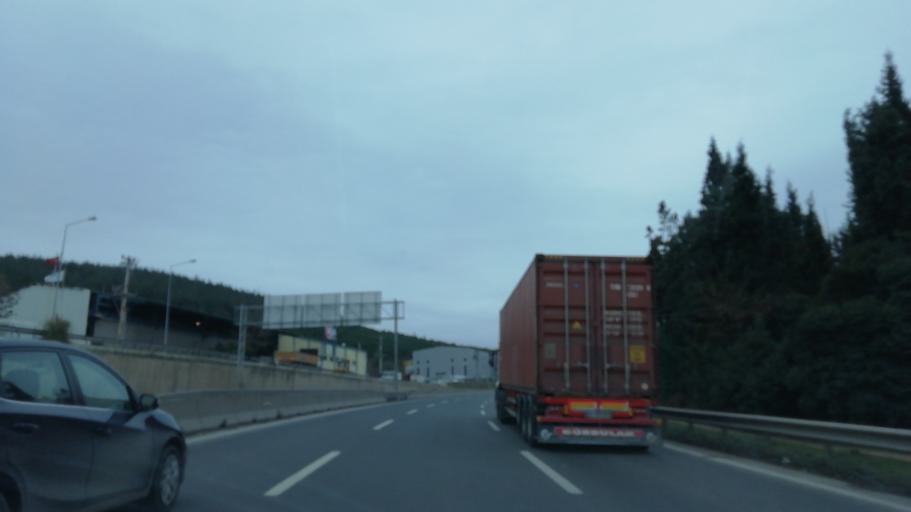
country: TR
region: Kocaeli
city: Tavsancil
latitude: 40.7787
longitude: 29.5452
